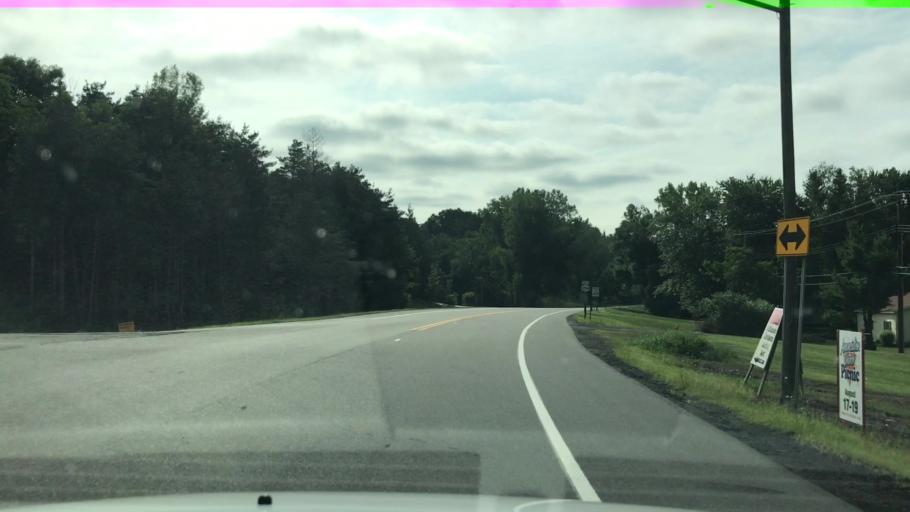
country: US
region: New York
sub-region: Erie County
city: Alden
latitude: 42.8571
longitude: -78.4992
